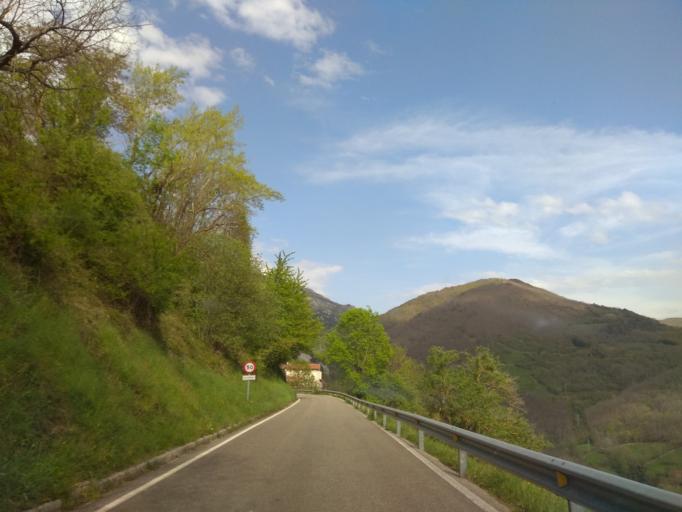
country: ES
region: Cantabria
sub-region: Provincia de Cantabria
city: Tresviso
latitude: 43.2521
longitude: -4.5861
